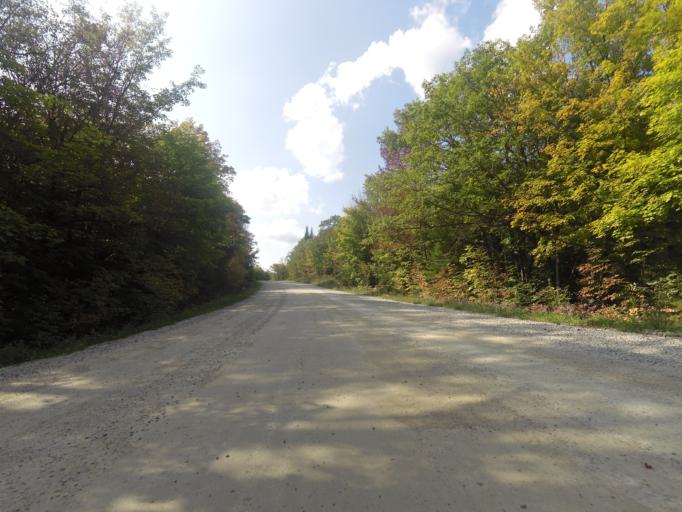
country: CA
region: Ontario
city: Renfrew
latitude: 45.1482
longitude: -76.6756
